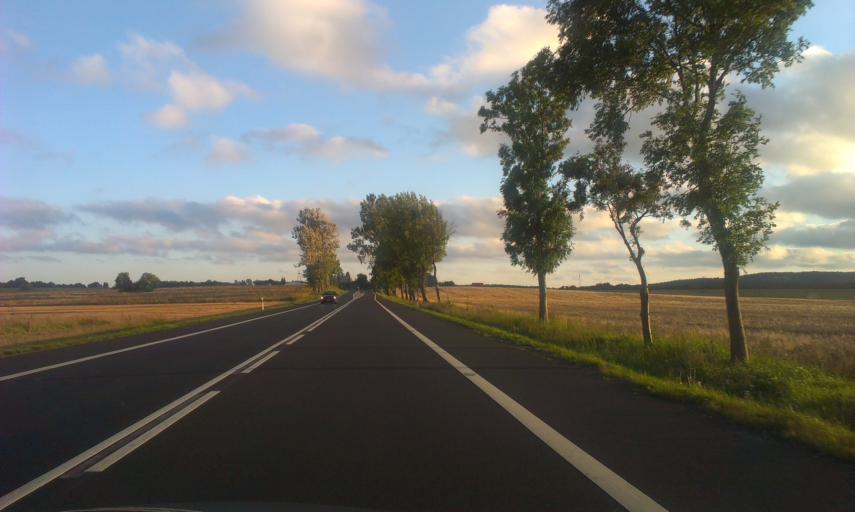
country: PL
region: West Pomeranian Voivodeship
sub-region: Powiat slawienski
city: Darlowo
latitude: 54.2868
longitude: 16.4902
